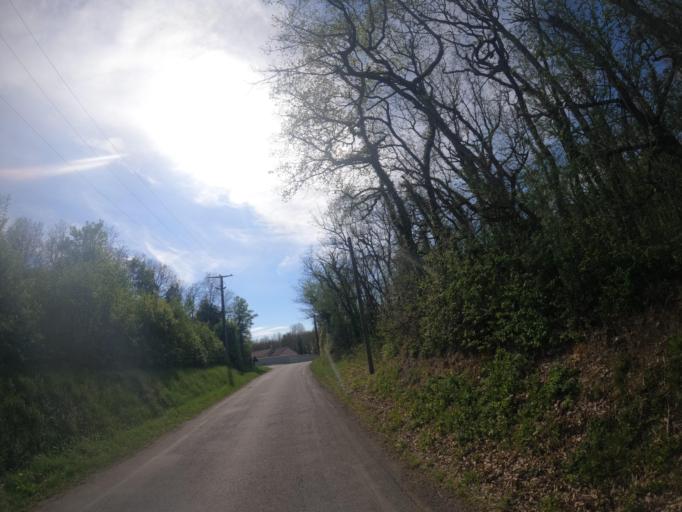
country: FR
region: Poitou-Charentes
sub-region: Departement des Deux-Sevres
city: Saint-Varent
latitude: 46.9171
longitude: -0.2067
